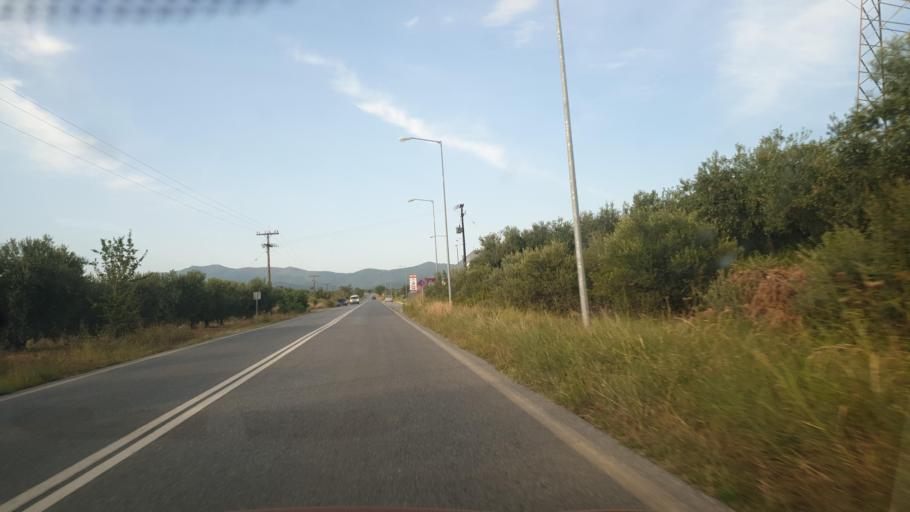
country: GR
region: Central Macedonia
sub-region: Nomos Chalkidikis
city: Kalyves Polygyrou
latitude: 40.3123
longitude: 23.4415
